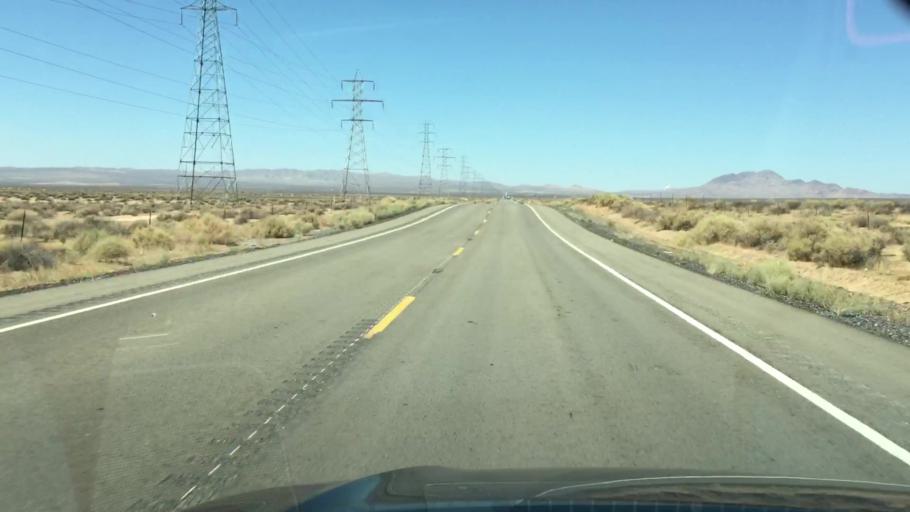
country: US
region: California
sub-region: Kern County
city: Boron
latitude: 35.1717
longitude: -117.5916
